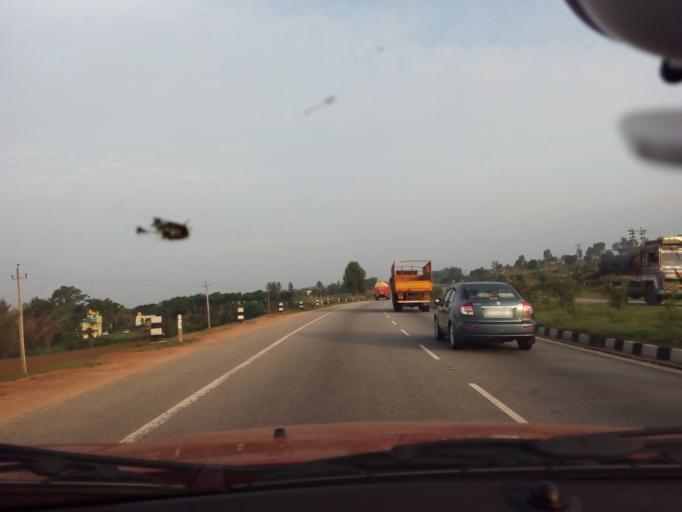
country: IN
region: Karnataka
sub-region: Bangalore Rural
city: Nelamangala
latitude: 13.0622
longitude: 77.2936
